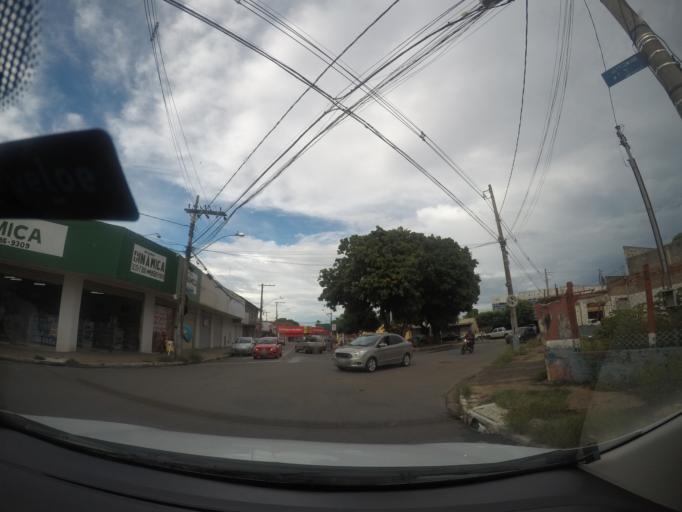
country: BR
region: Goias
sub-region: Goiania
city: Goiania
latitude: -16.6689
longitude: -49.2812
